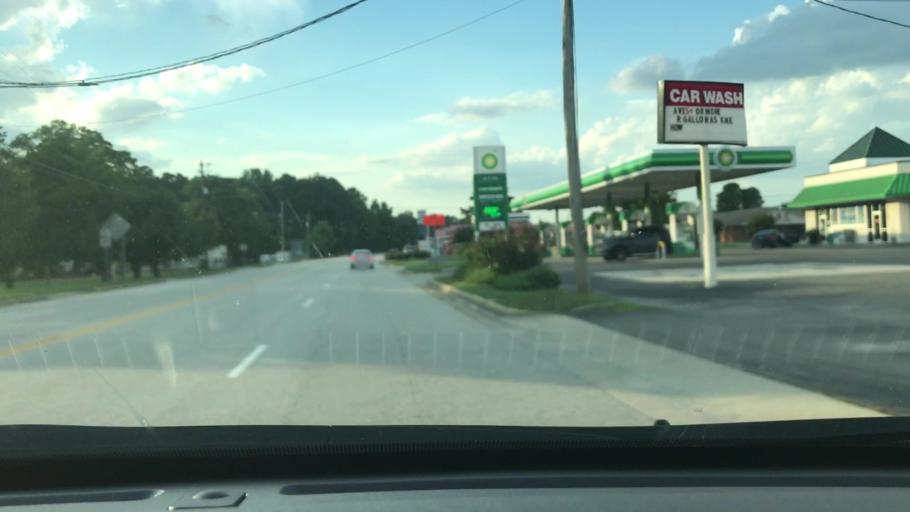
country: US
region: North Carolina
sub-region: Harnett County
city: Dunn
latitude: 35.2937
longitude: -78.6051
